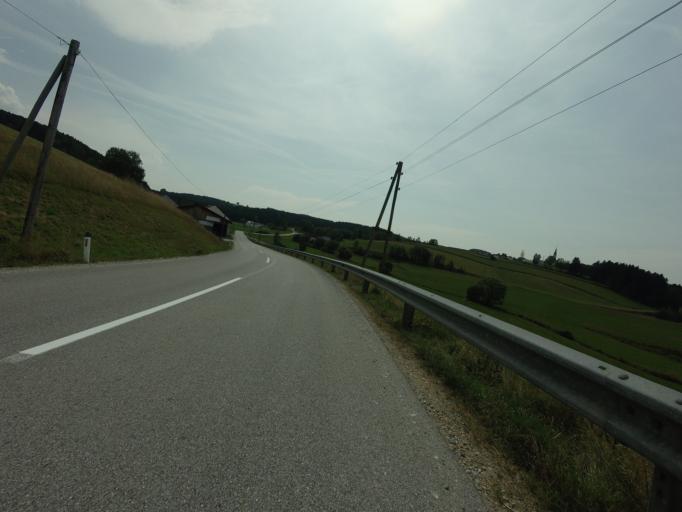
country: AT
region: Upper Austria
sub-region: Politischer Bezirk Urfahr-Umgebung
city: Reichenthal
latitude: 48.5491
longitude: 14.3965
